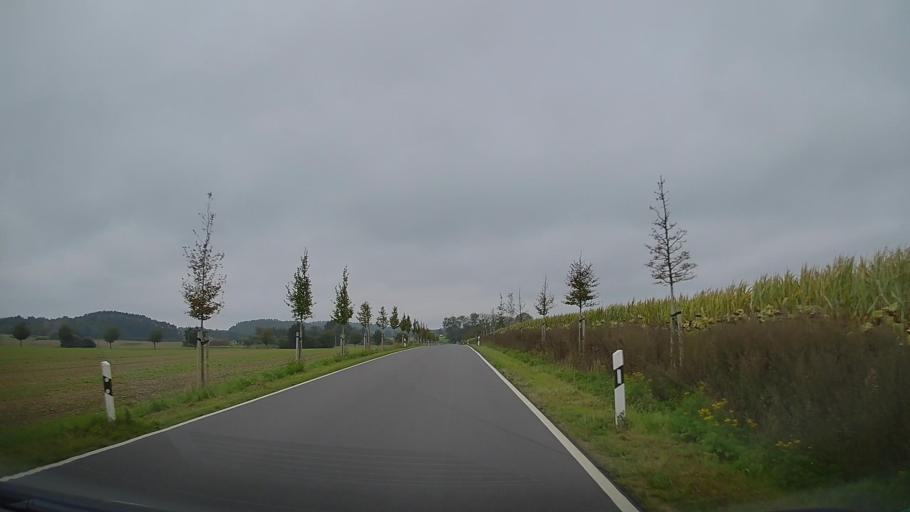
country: DE
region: Mecklenburg-Vorpommern
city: Dummerstorf
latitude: 53.9555
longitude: 12.2318
